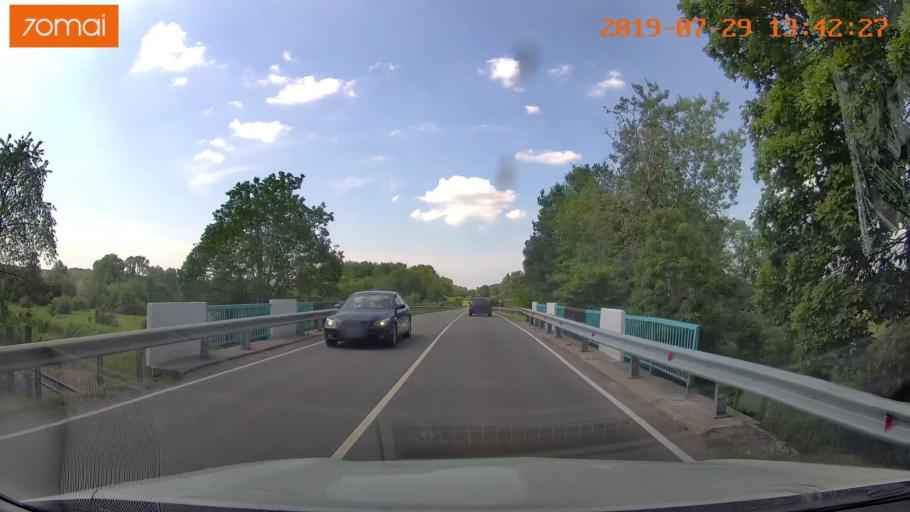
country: RU
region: Kaliningrad
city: Svetlyy
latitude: 54.7368
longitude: 20.1119
